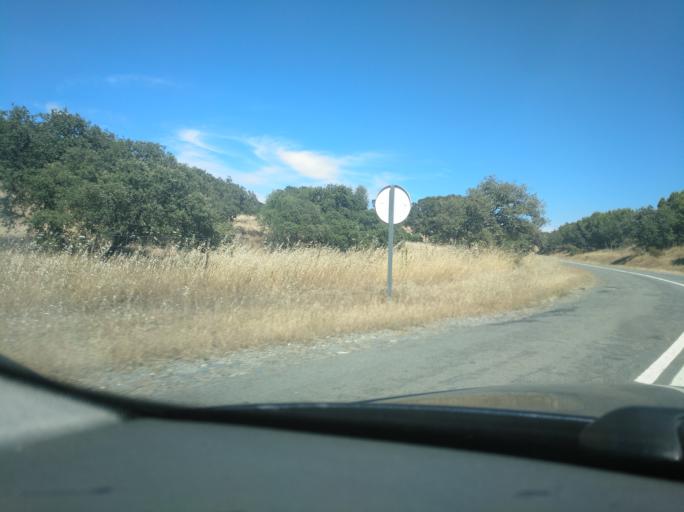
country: PT
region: Beja
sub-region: Almodovar
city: Almodovar
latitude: 37.5398
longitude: -7.9913
